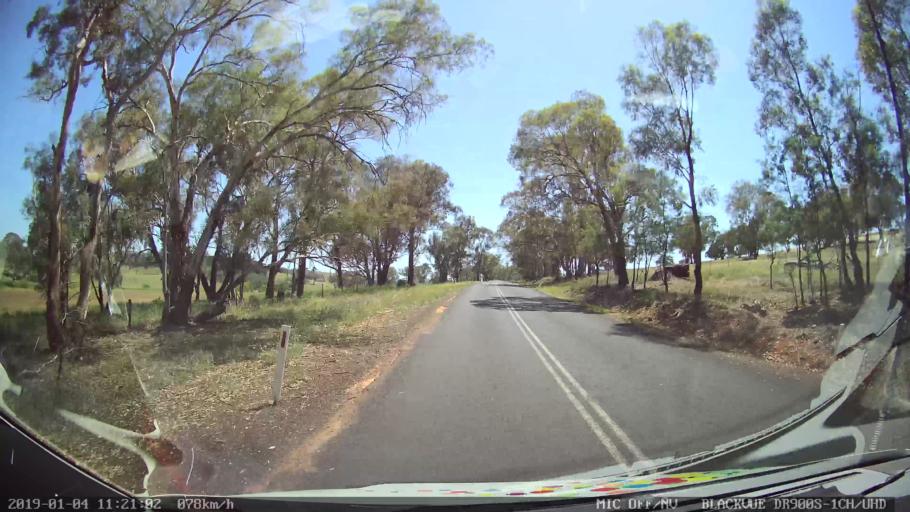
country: AU
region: New South Wales
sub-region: Cabonne
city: Molong
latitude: -33.1575
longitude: 148.7066
